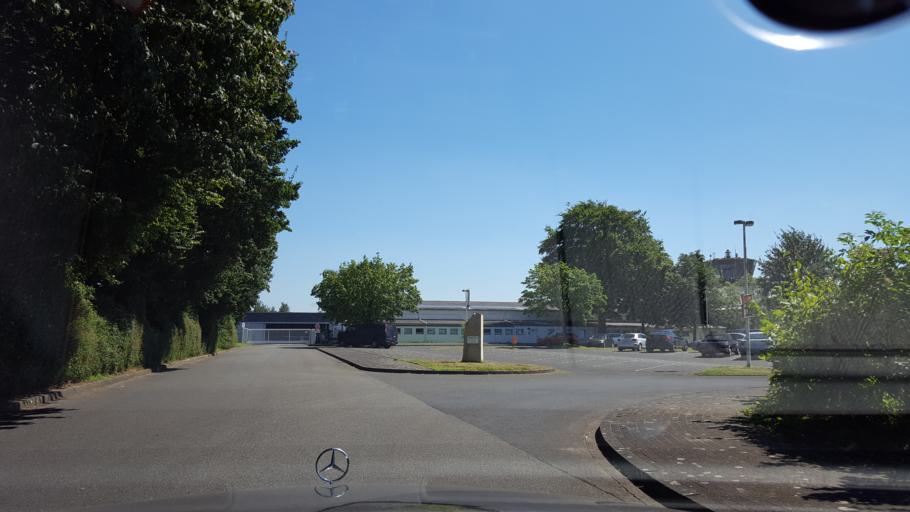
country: DE
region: North Rhine-Westphalia
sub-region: Regierungsbezirk Munster
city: Recklinghausen
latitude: 51.6479
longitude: 7.1580
